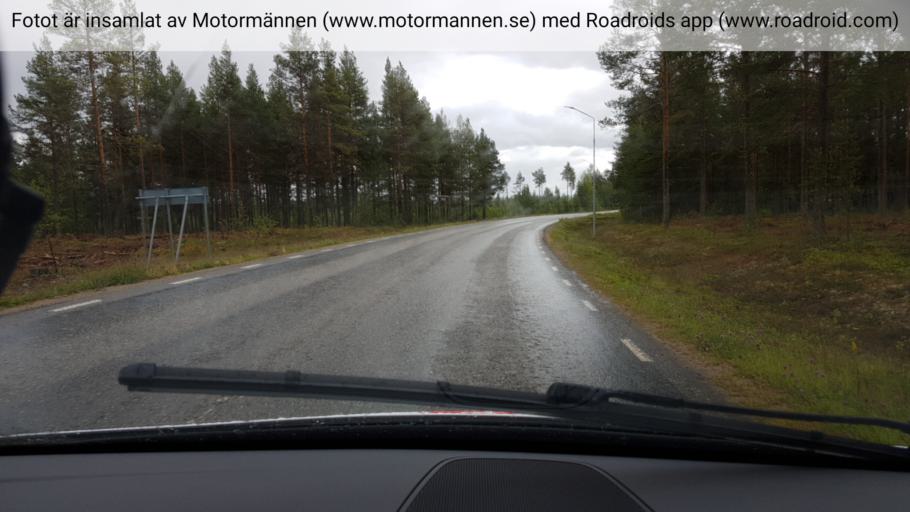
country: SE
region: Jaemtland
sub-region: Harjedalens Kommun
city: Sveg
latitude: 62.4423
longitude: 13.8764
